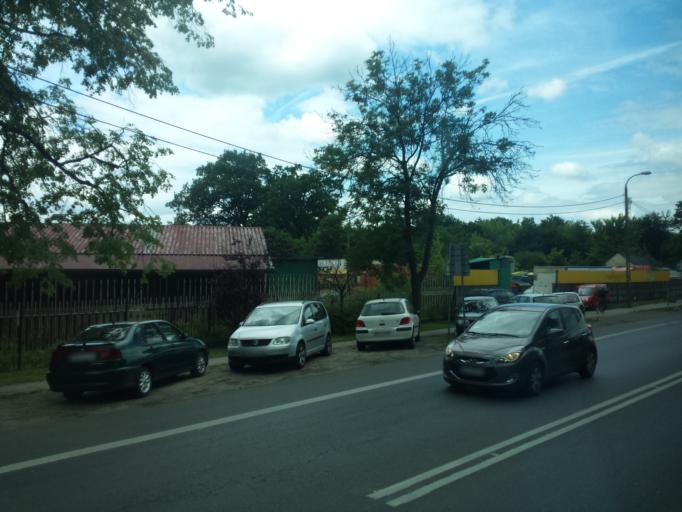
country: PL
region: Masovian Voivodeship
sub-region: Powiat minski
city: Sulejowek
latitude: 52.2219
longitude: 21.2506
